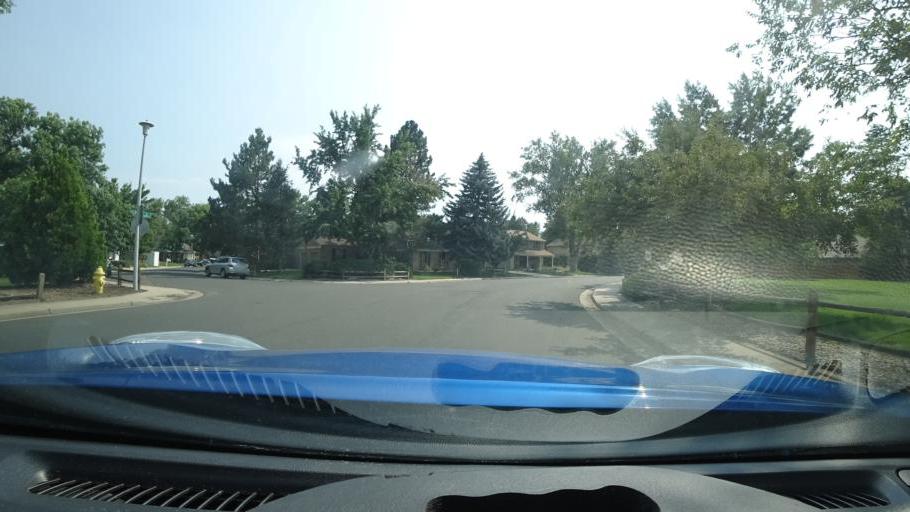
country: US
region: Colorado
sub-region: Adams County
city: Aurora
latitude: 39.6644
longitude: -104.8481
